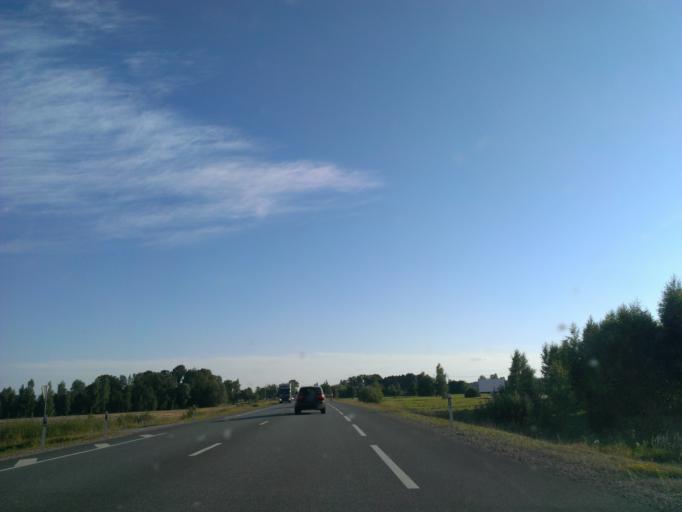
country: LV
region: Adazi
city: Adazi
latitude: 57.1049
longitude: 24.3144
